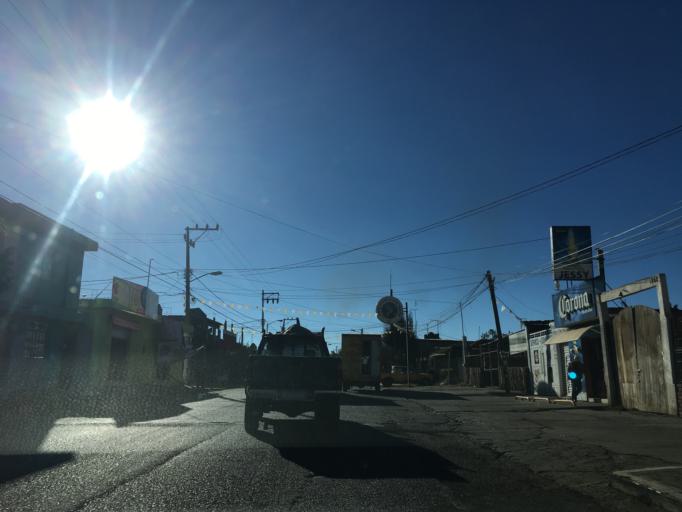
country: MX
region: Michoacan
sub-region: Morelia
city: Montana Monarca (Punta Altozano)
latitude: 19.6601
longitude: -101.1585
